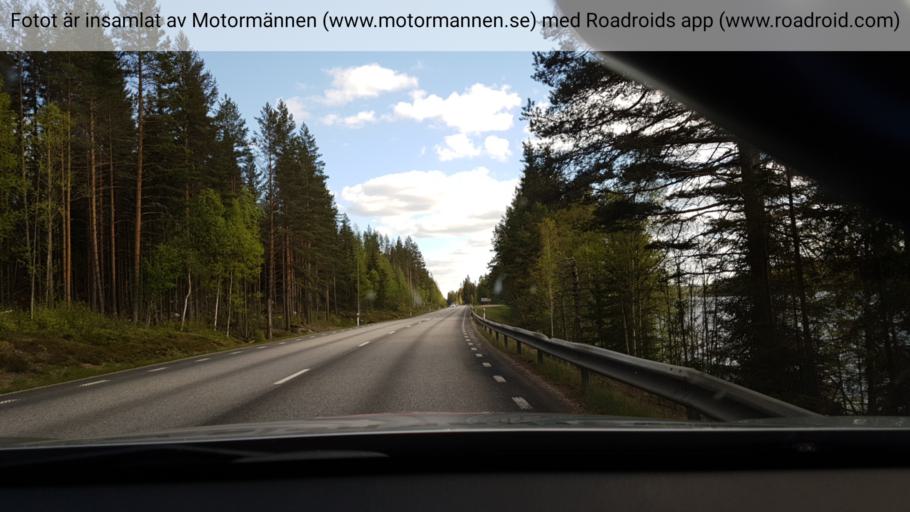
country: SE
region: Dalarna
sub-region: Faluns Kommun
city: Bjursas
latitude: 60.7759
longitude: 15.3165
